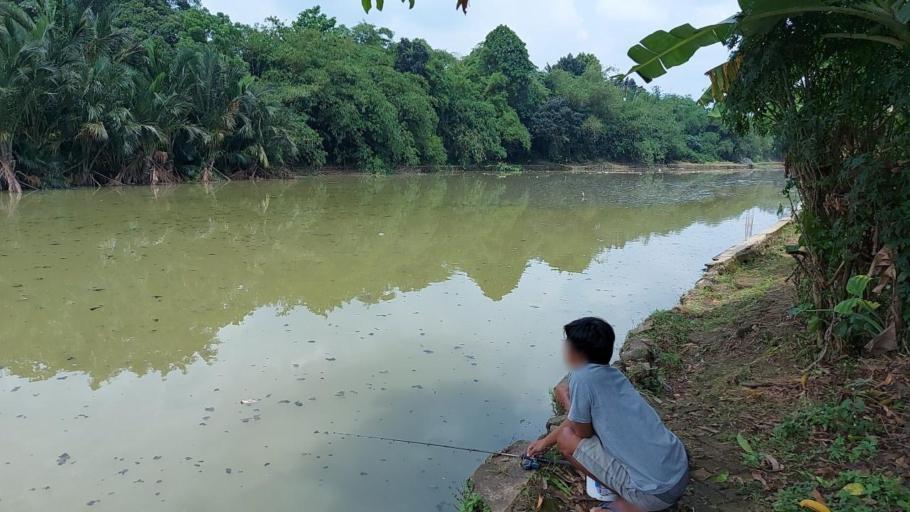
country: ID
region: West Java
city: Cibinong
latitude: -6.4663
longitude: 106.8097
